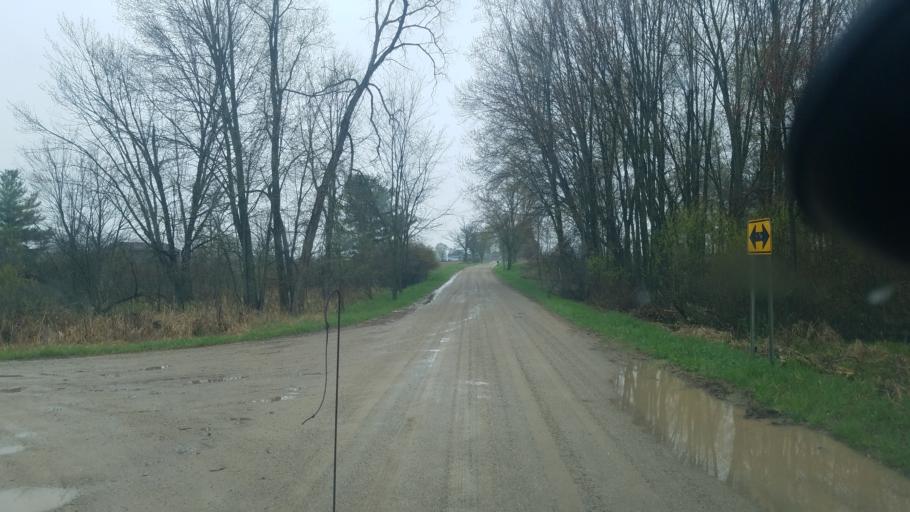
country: US
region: Michigan
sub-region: Montcalm County
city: Lakeview
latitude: 43.4681
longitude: -85.3332
